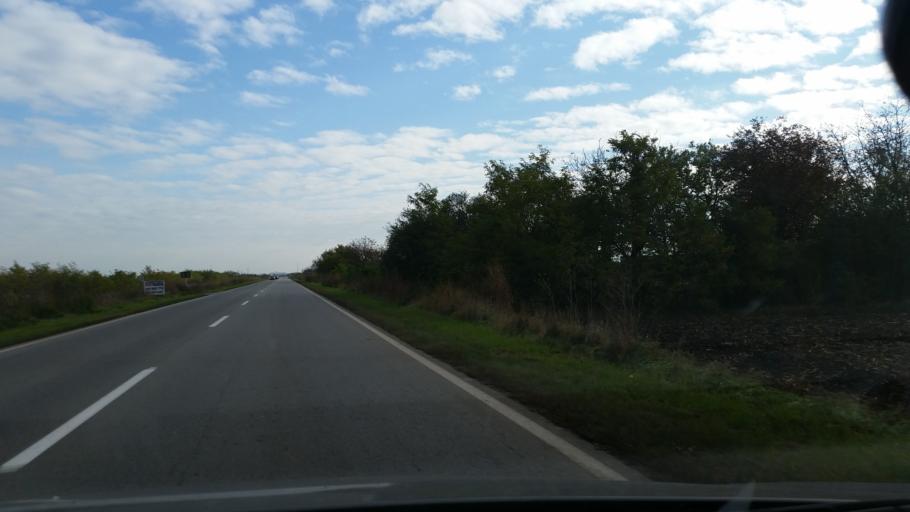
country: RS
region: Autonomna Pokrajina Vojvodina
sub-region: Srednjebanatski Okrug
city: Zrenjanin
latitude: 45.4323
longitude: 20.3676
